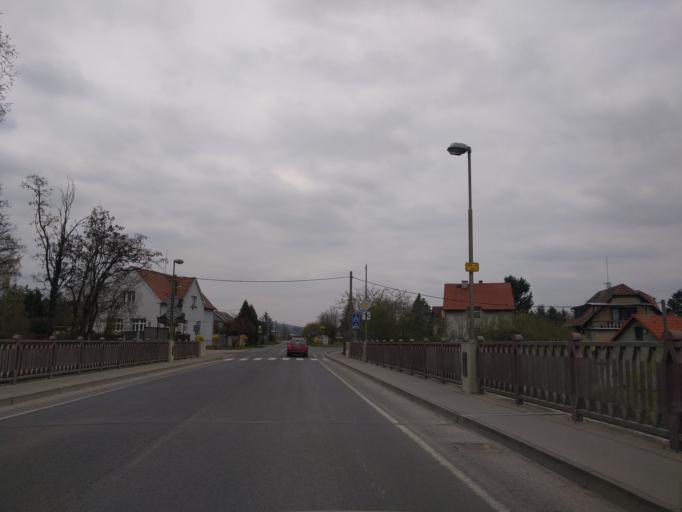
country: CZ
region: Central Bohemia
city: Revnice
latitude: 49.9193
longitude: 14.2485
